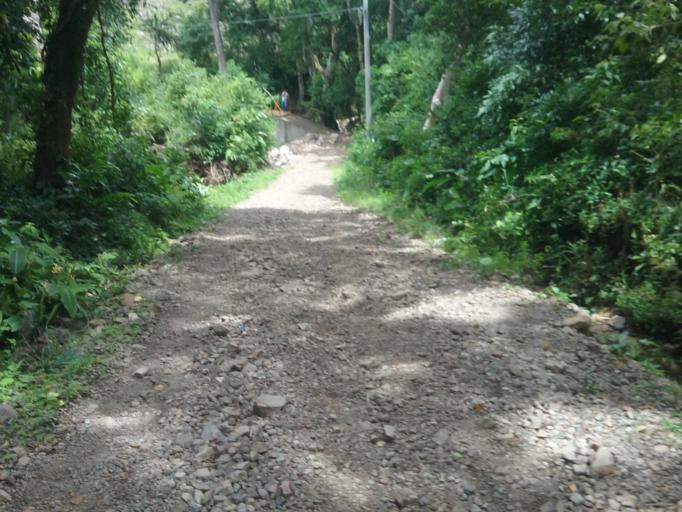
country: NI
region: Matagalpa
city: Matagalpa
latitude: 12.8690
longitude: -85.9171
